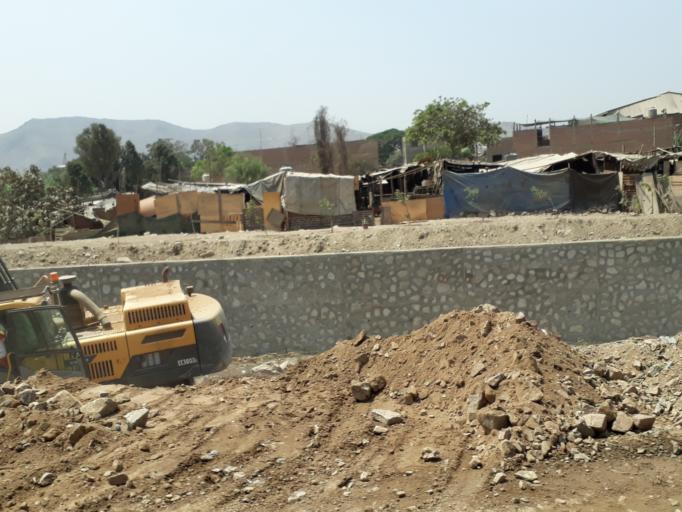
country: PE
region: Lima
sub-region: Lima
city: Santa Maria
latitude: -11.9946
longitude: -76.9097
